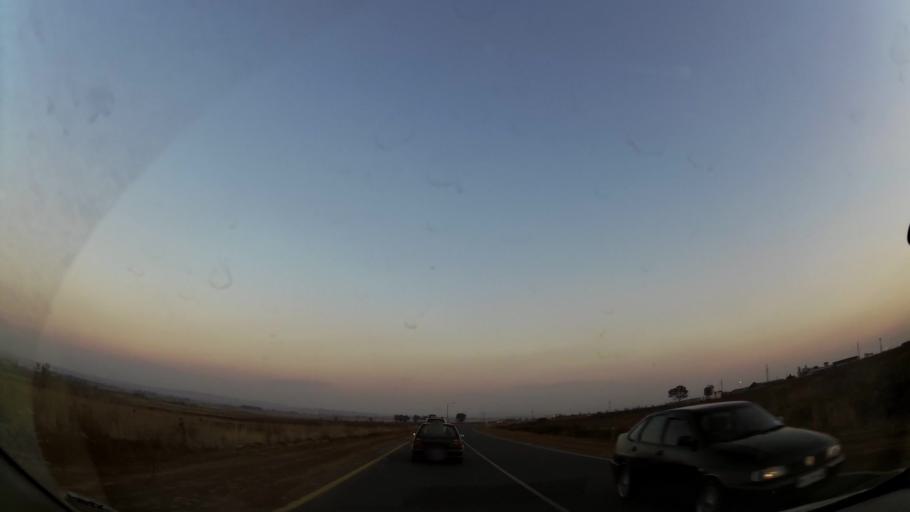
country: ZA
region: Gauteng
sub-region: Ekurhuleni Metropolitan Municipality
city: Nigel
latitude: -26.3705
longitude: 28.4214
